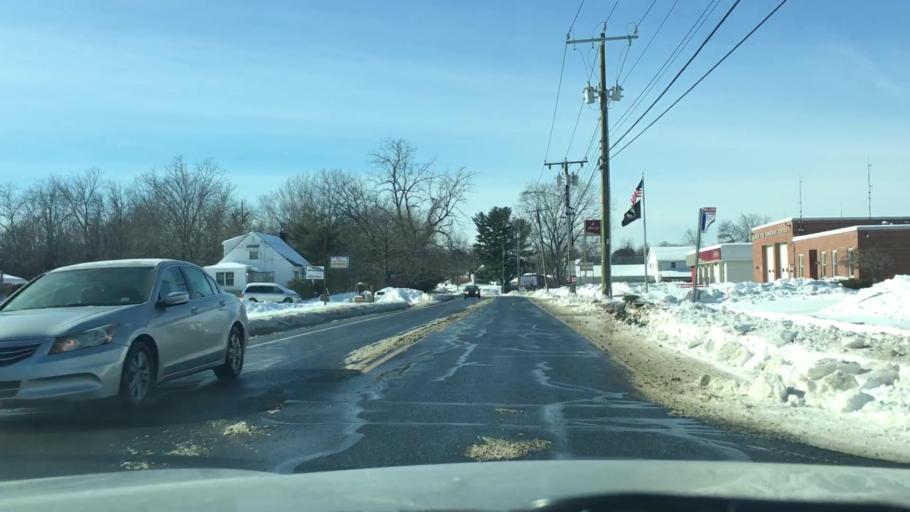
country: US
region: Massachusetts
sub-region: Hampden County
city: Agawam
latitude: 42.0684
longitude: -72.6700
